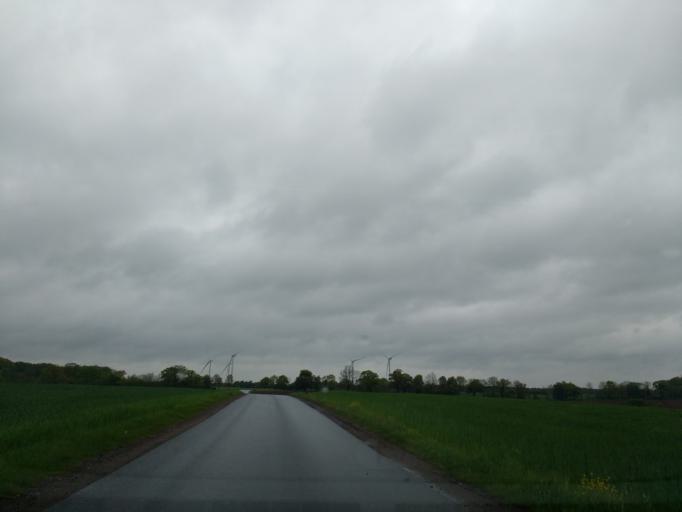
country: DE
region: Schleswig-Holstein
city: Loose
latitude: 54.5060
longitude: 9.9227
